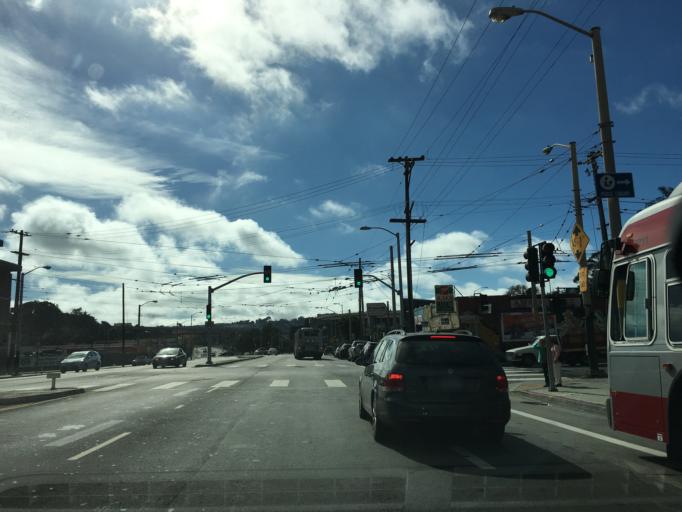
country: US
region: California
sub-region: San Francisco County
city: San Francisco
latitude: 37.7399
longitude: -122.4070
